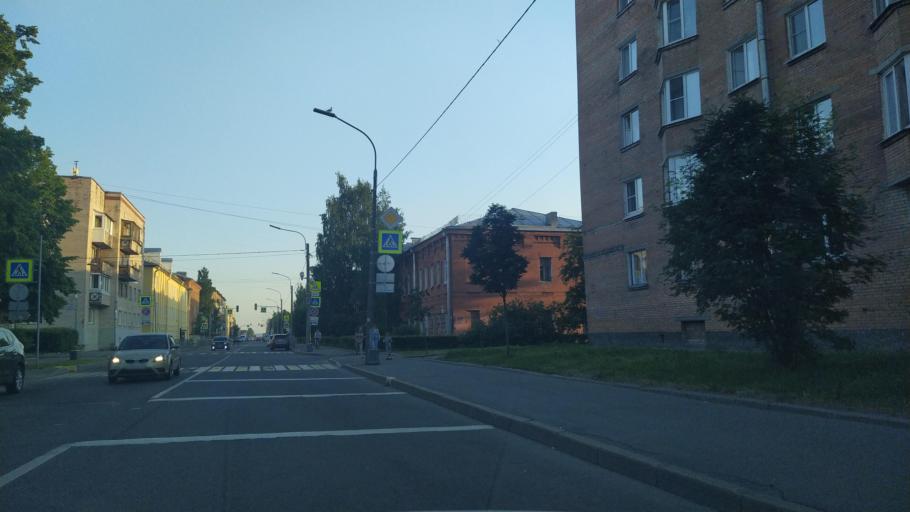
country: RU
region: St.-Petersburg
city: Kronshtadt
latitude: 59.9974
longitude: 29.7592
